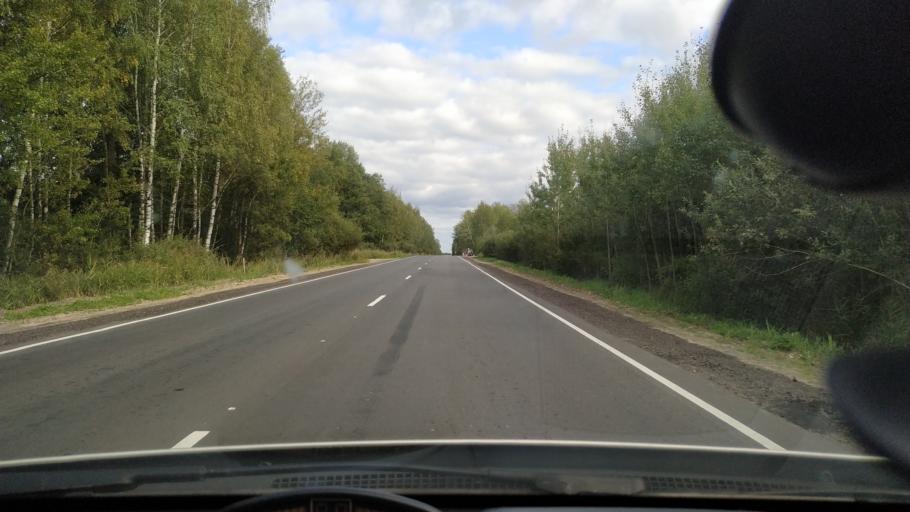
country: RU
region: Moskovskaya
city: Likino-Dulevo
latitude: 55.7276
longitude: 39.0291
